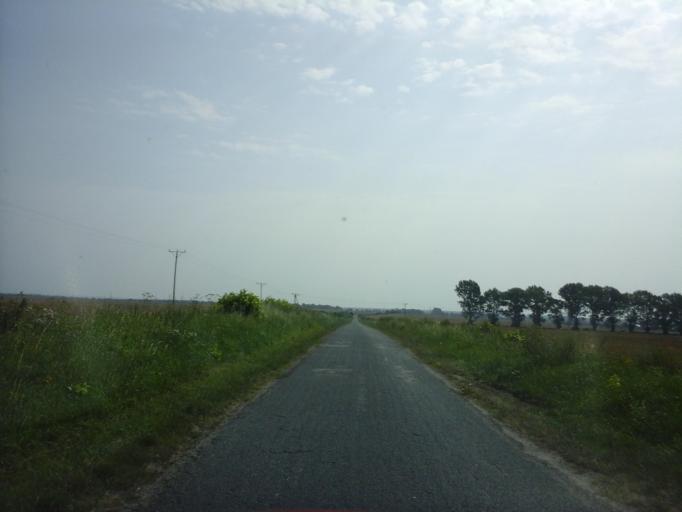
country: PL
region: West Pomeranian Voivodeship
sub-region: Powiat choszczenski
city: Pelczyce
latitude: 53.0487
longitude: 15.2715
